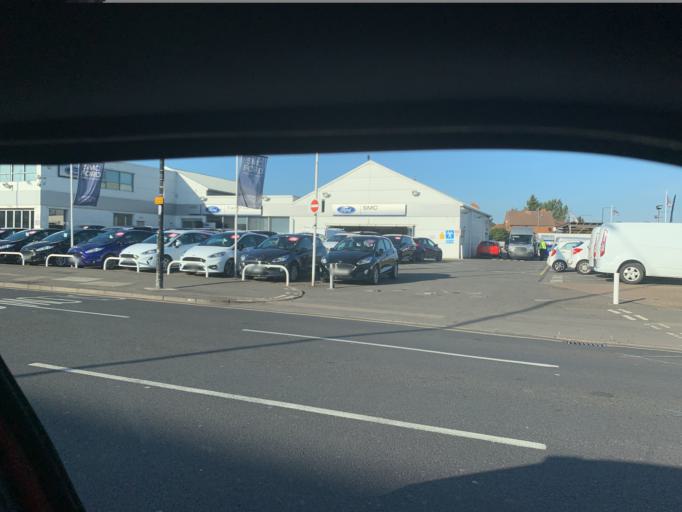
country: GB
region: England
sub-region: Slough
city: Slough
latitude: 51.5127
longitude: -0.6134
